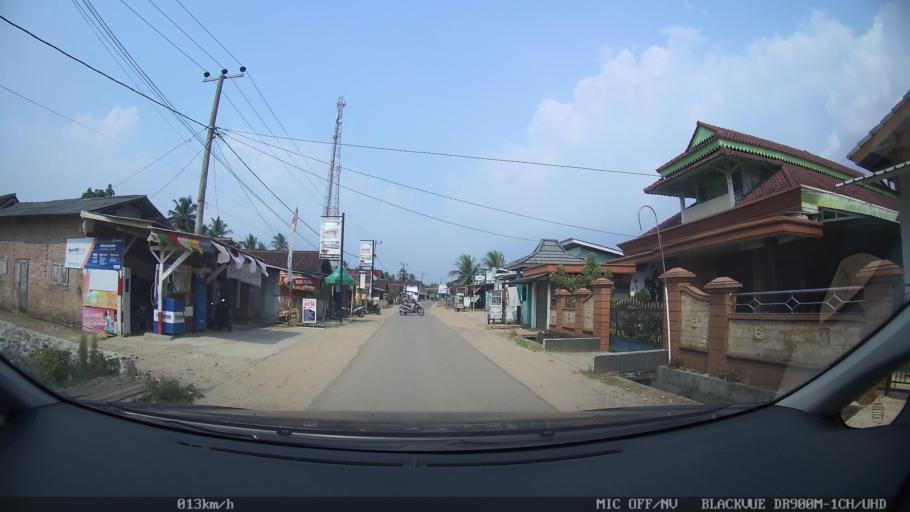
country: ID
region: Lampung
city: Kedondong
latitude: -5.4106
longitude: 104.9937
